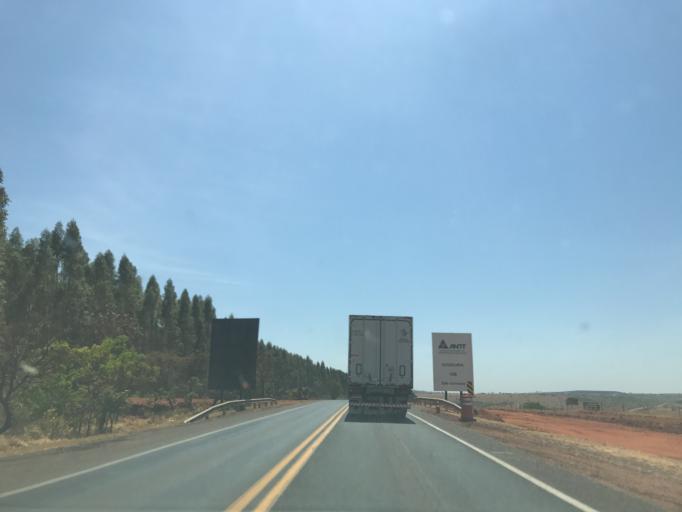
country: BR
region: Minas Gerais
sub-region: Prata
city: Prata
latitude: -19.4509
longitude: -48.8856
